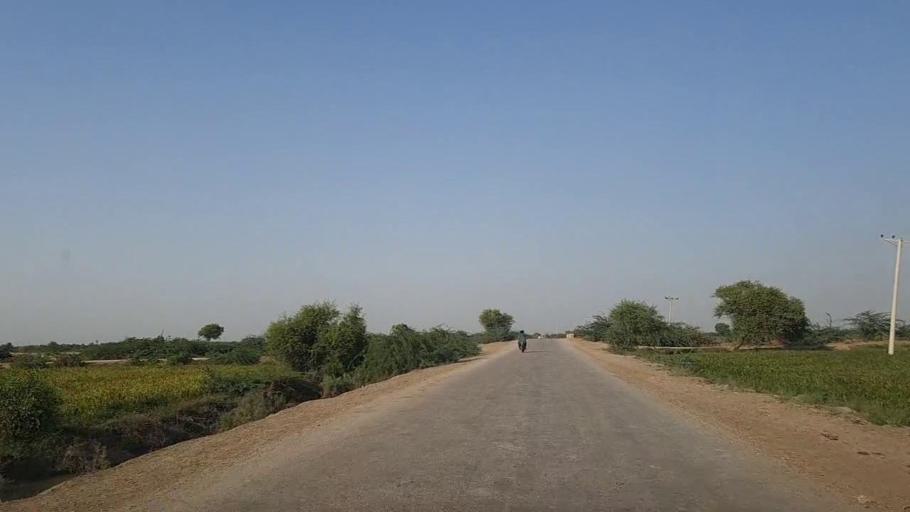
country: PK
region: Sindh
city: Mirpur Batoro
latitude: 24.5984
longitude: 68.4001
